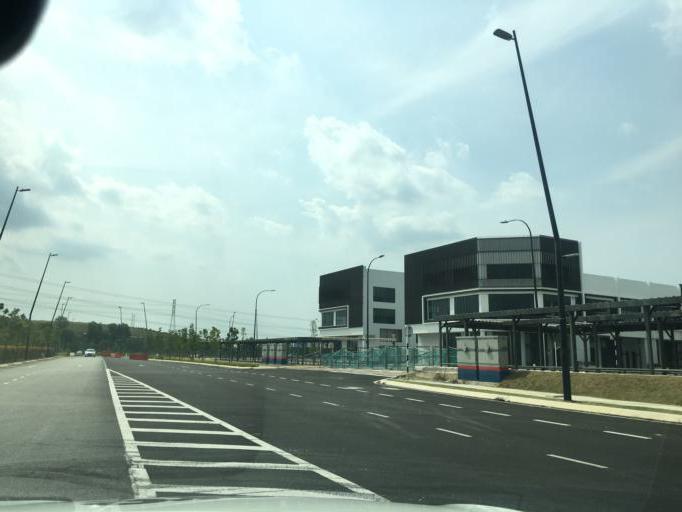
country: MY
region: Selangor
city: Shah Alam
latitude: 3.0859
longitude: 101.4760
